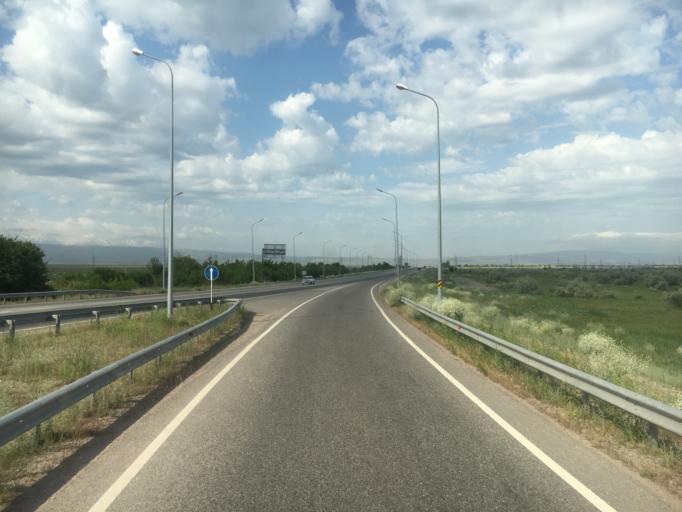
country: KZ
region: Zhambyl
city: Taraz
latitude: 42.8216
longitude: 71.1600
